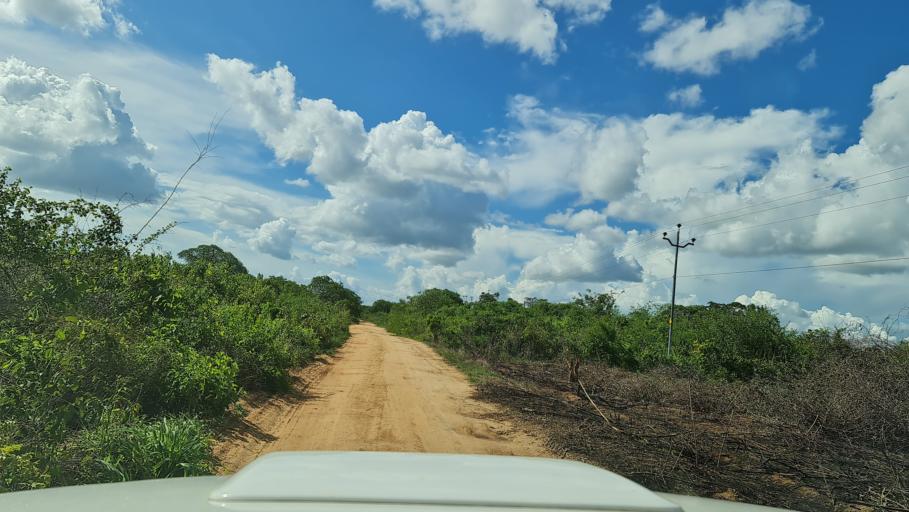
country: MZ
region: Nampula
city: Ilha de Mocambique
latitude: -15.4303
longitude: 40.2737
